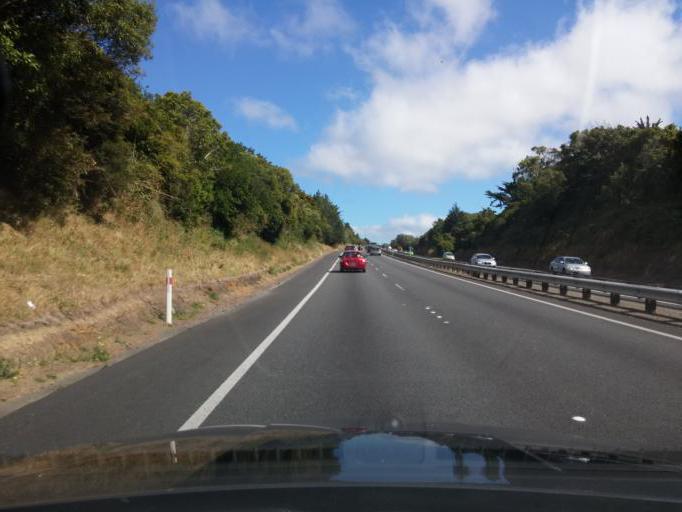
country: NZ
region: Wellington
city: Petone
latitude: -41.2106
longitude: 174.8156
